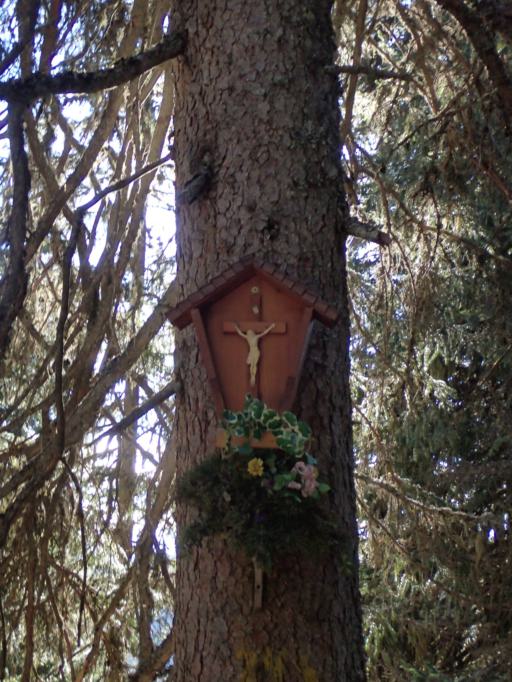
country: AT
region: Salzburg
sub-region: Politischer Bezirk Sankt Johann im Pongau
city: Muhlbach am Hochkonig
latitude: 47.3677
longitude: 13.0869
